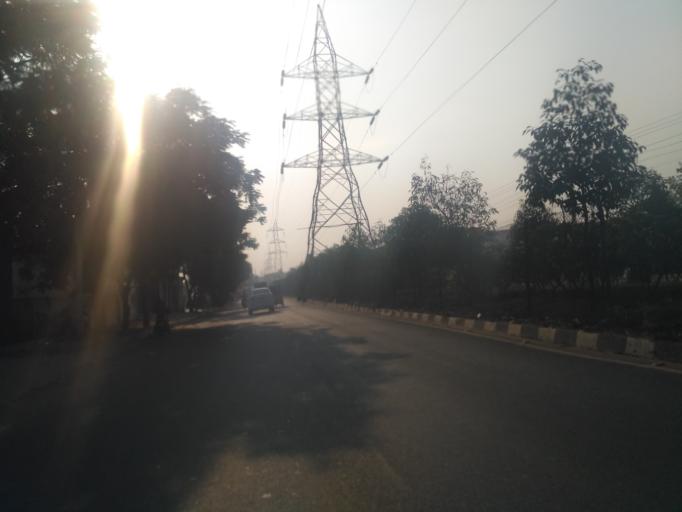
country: IN
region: Telangana
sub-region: Rangareddi
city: Kukatpalli
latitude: 17.4517
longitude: 78.3951
